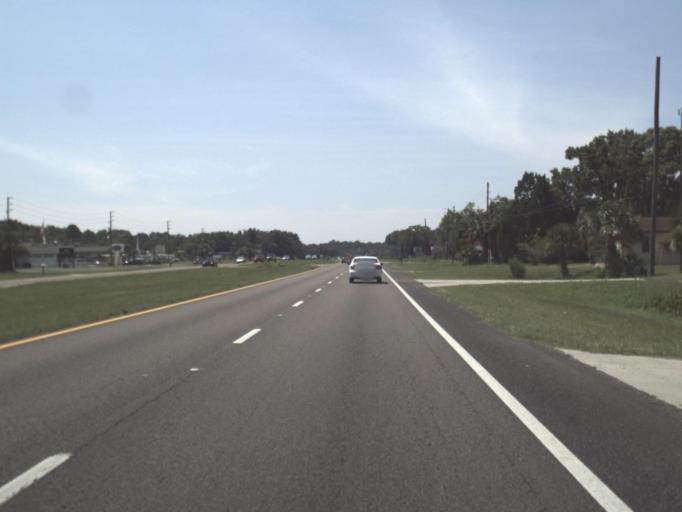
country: US
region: Florida
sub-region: Citrus County
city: Homosassa Springs
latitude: 28.7900
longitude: -82.5672
